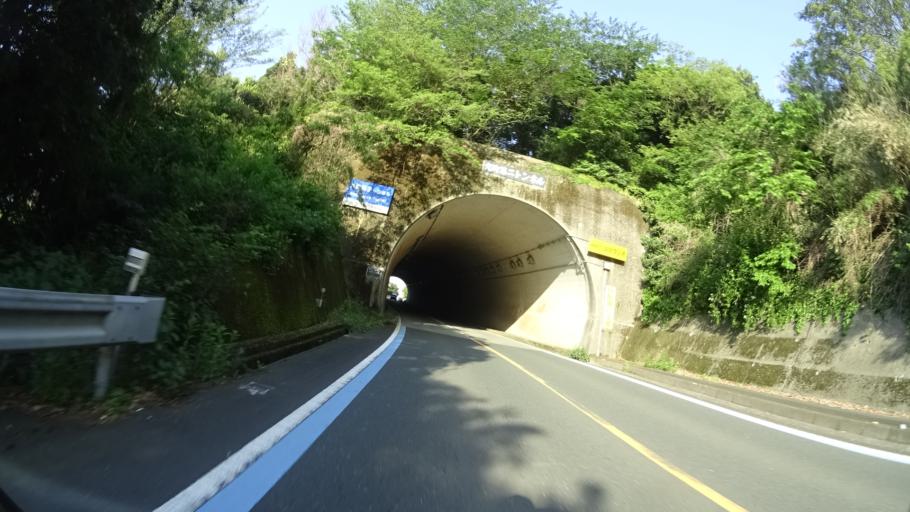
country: JP
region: Ehime
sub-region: Nishiuwa-gun
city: Ikata-cho
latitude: 33.4829
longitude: 132.3176
